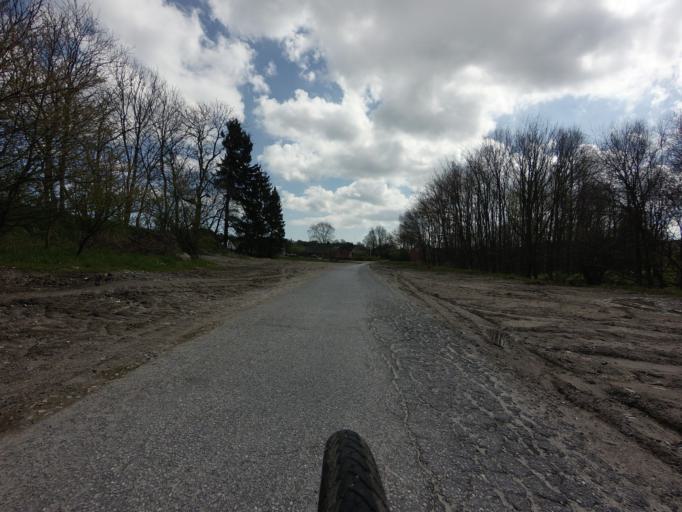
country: DK
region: North Denmark
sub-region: Mariagerfjord Kommune
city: Hadsund
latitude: 56.8328
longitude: 10.1218
